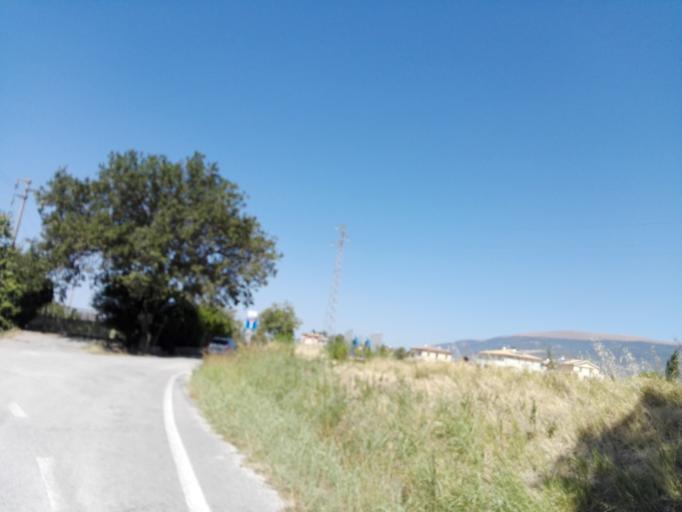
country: IT
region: Umbria
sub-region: Provincia di Perugia
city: Foligno
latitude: 42.9493
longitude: 12.6828
